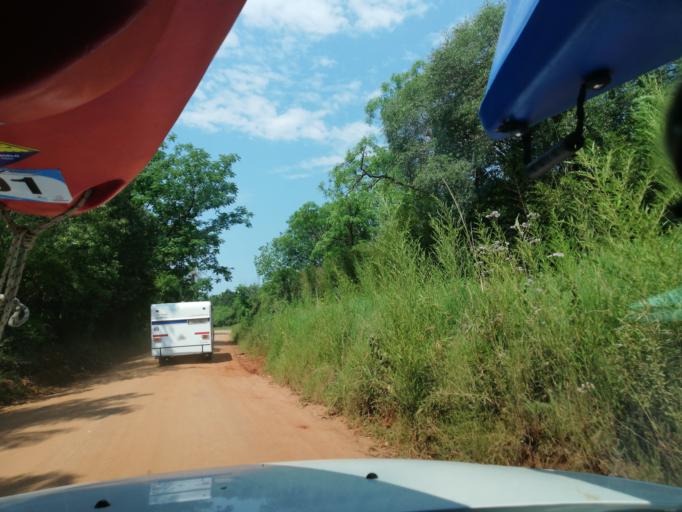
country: AR
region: Misiones
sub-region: Departamento de San Ignacio
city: San Ignacio
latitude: -27.2644
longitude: -55.5515
